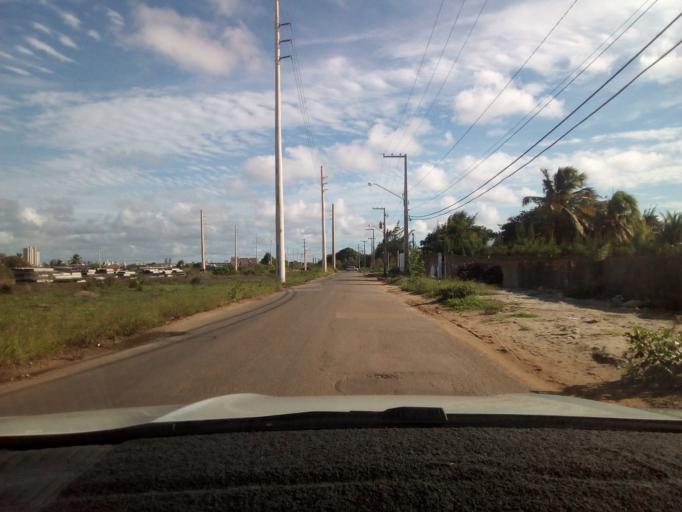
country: BR
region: Paraiba
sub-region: Cabedelo
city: Cabedelo
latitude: -7.0385
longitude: -34.8510
